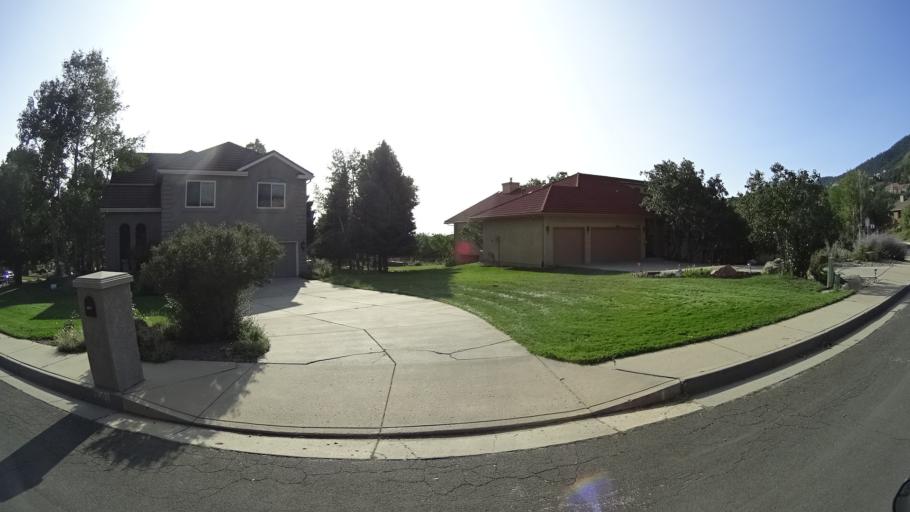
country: US
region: Colorado
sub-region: El Paso County
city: Manitou Springs
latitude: 38.8238
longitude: -104.8814
